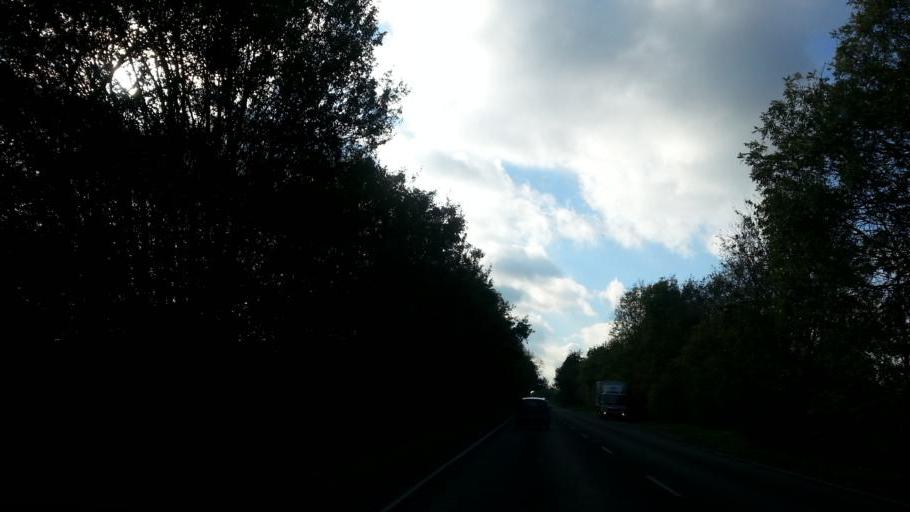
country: GB
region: England
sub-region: Suffolk
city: Bungay
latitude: 52.4557
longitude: 1.4245
